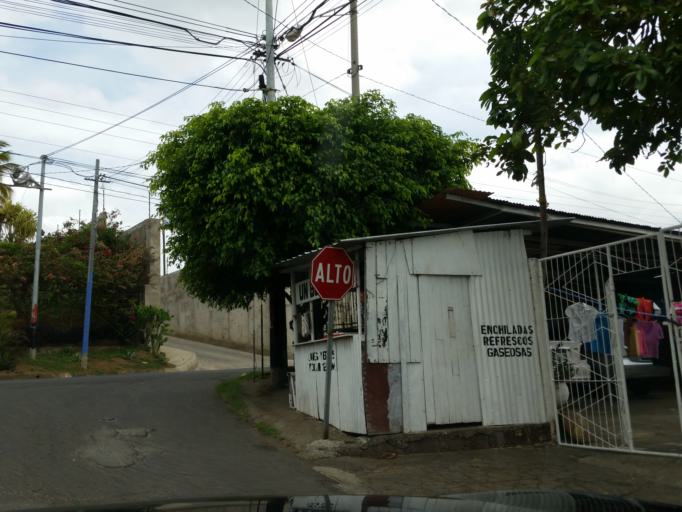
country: NI
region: Managua
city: Managua
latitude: 12.0908
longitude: -86.2451
